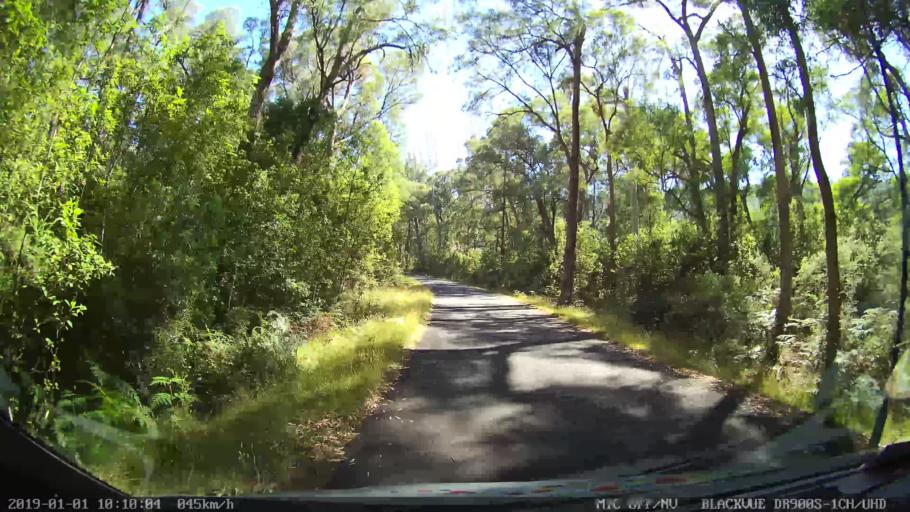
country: AU
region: New South Wales
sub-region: Snowy River
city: Jindabyne
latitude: -36.1438
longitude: 148.1579
